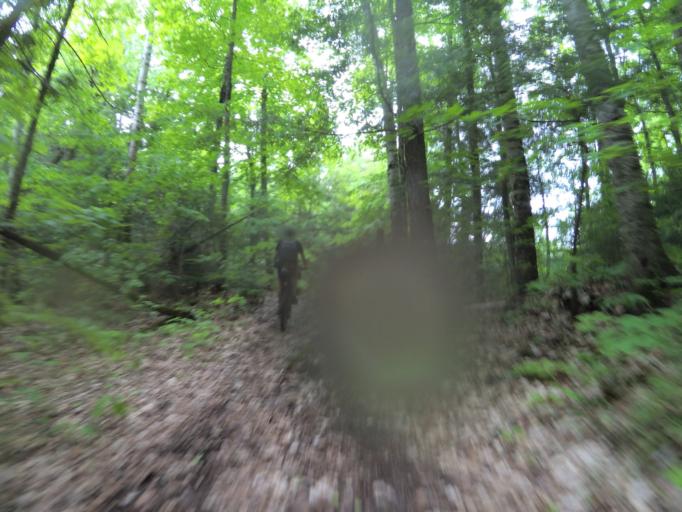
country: CA
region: Ontario
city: Renfrew
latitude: 45.0731
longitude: -76.9007
